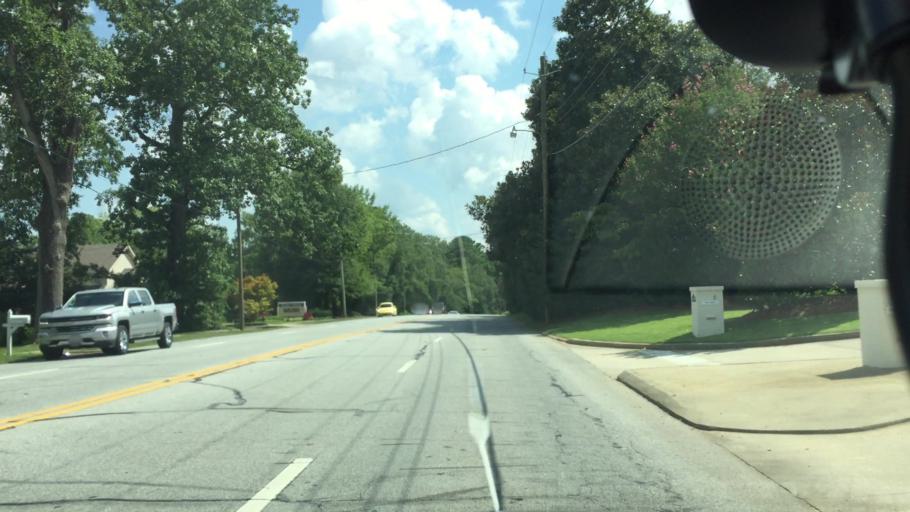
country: US
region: Alabama
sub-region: Lee County
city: Auburn
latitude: 32.5979
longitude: -85.4818
